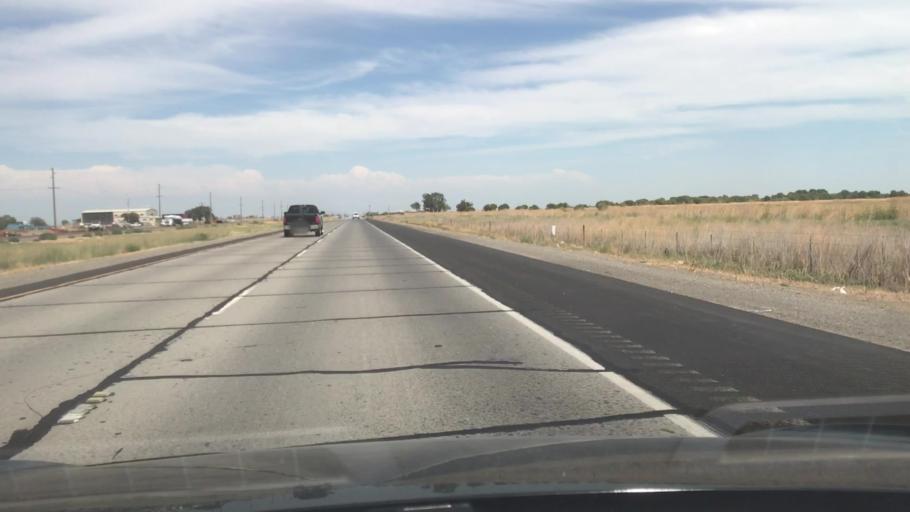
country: US
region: California
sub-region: Merced County
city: Los Banos
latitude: 37.0557
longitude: -120.7957
